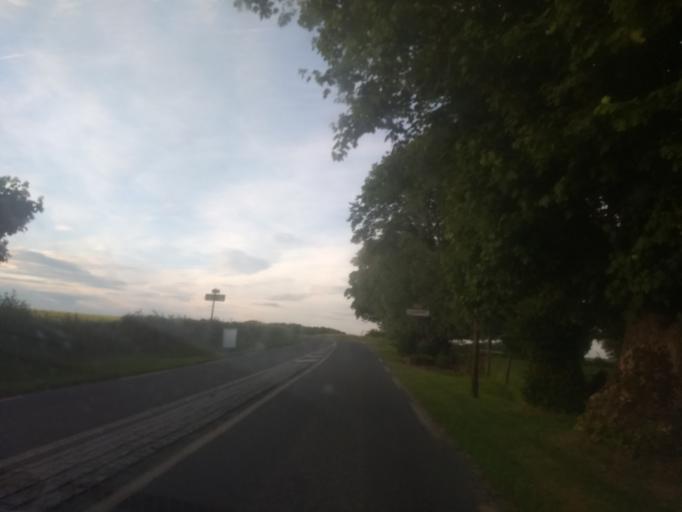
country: FR
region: Nord-Pas-de-Calais
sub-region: Departement du Pas-de-Calais
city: Bucquoy
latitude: 50.1225
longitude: 2.6939
